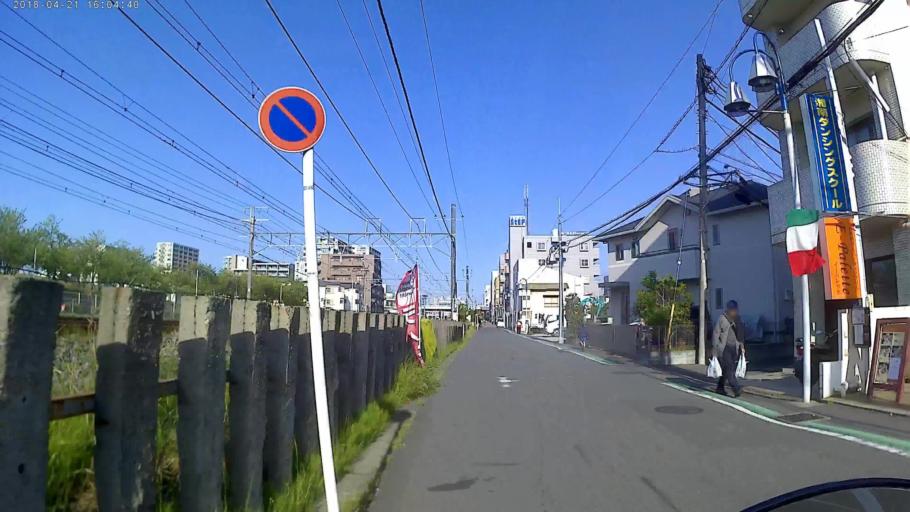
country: JP
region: Kanagawa
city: Fujisawa
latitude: 35.3365
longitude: 139.4408
